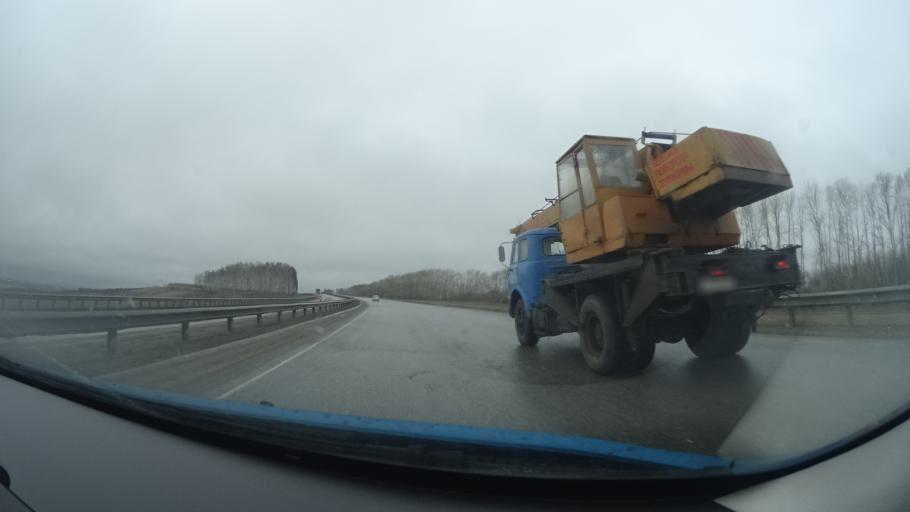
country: RU
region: Bashkortostan
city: Alekseyevka
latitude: 54.7392
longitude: 55.0960
